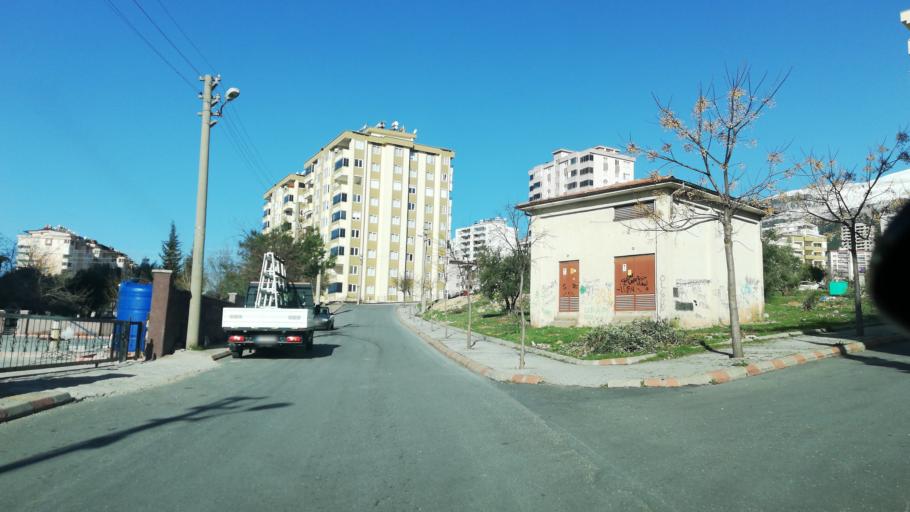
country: TR
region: Kahramanmaras
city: Kahramanmaras
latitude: 37.5950
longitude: 36.8943
